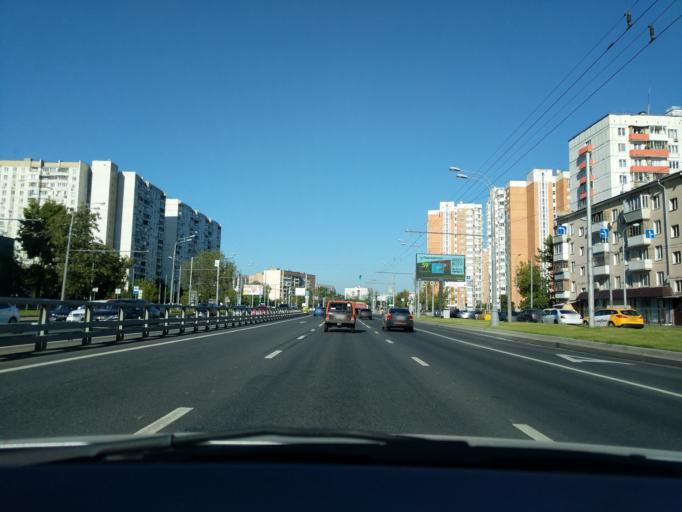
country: RU
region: Moscow
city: Metrogorodok
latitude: 55.8082
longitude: 37.7744
